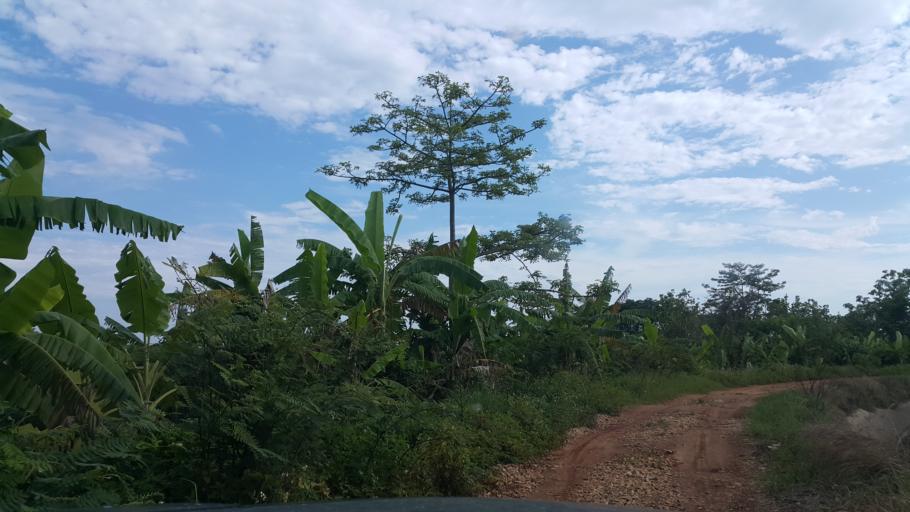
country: TH
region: Chiang Rai
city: Wiang Chai
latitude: 19.9710
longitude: 99.9068
